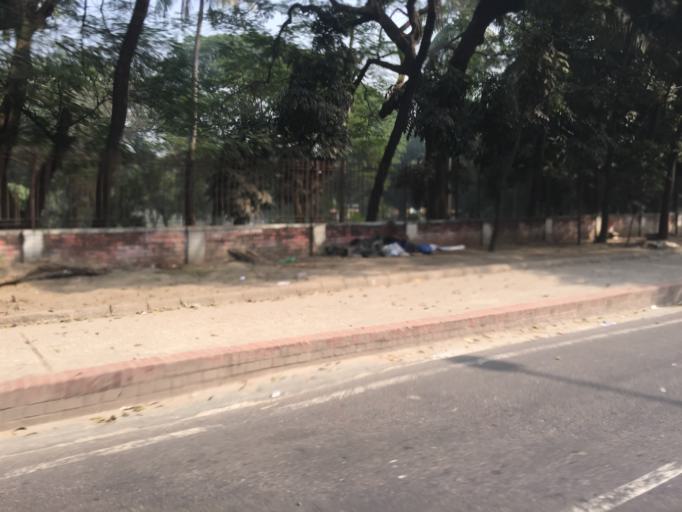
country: BD
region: Dhaka
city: Paltan
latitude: 23.7356
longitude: 90.4003
